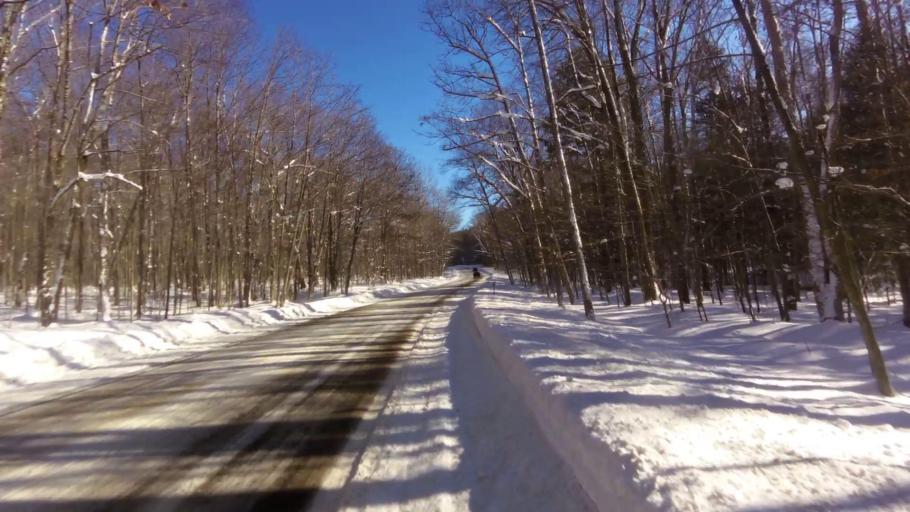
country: US
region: New York
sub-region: Cattaraugus County
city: Salamanca
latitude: 42.1244
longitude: -78.7249
